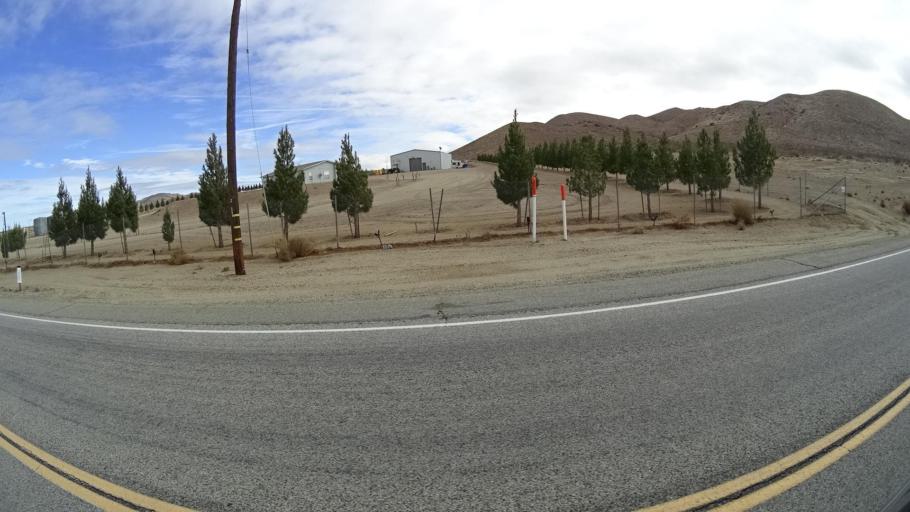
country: US
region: California
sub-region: Kern County
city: Rosamond
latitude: 34.8876
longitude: -118.2912
